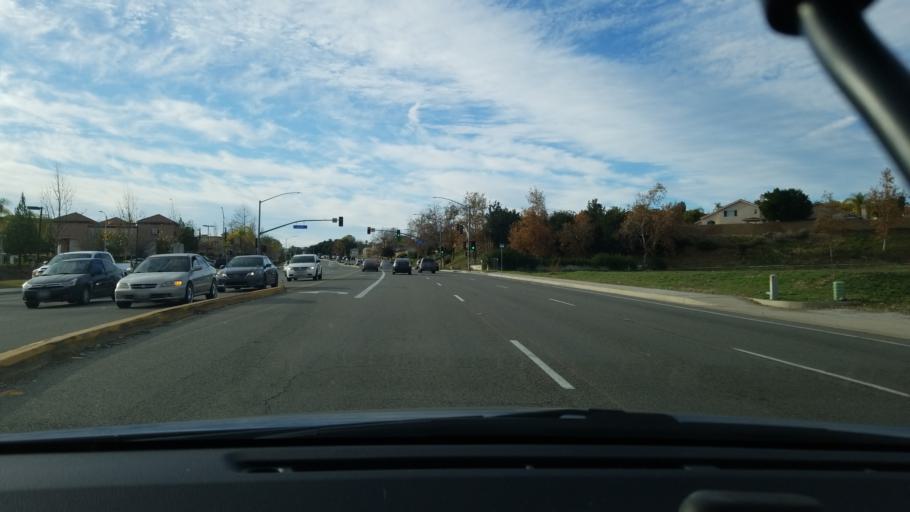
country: US
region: California
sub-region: Riverside County
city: Murrieta Hot Springs
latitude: 33.5556
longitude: -117.1718
